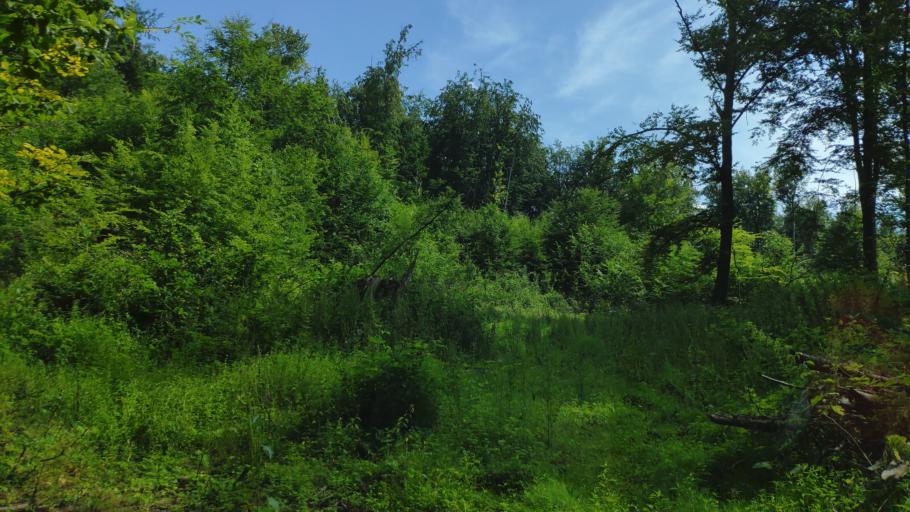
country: SK
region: Kosicky
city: Dobsina
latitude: 48.7113
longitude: 20.3875
